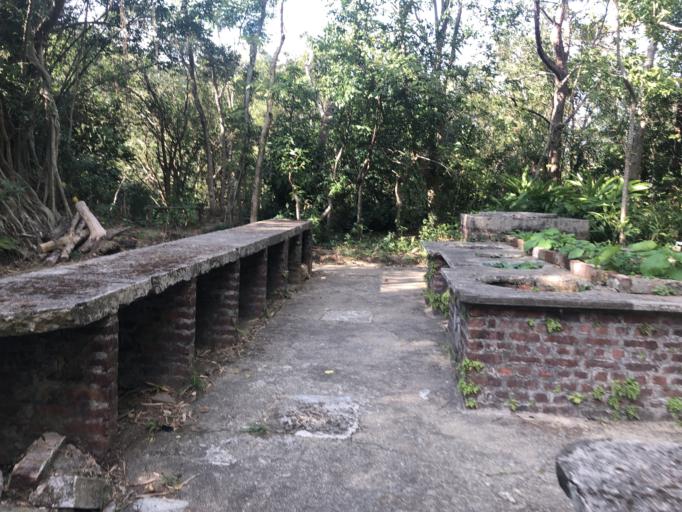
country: HK
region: Wanchai
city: Wan Chai
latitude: 22.2759
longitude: 114.2133
